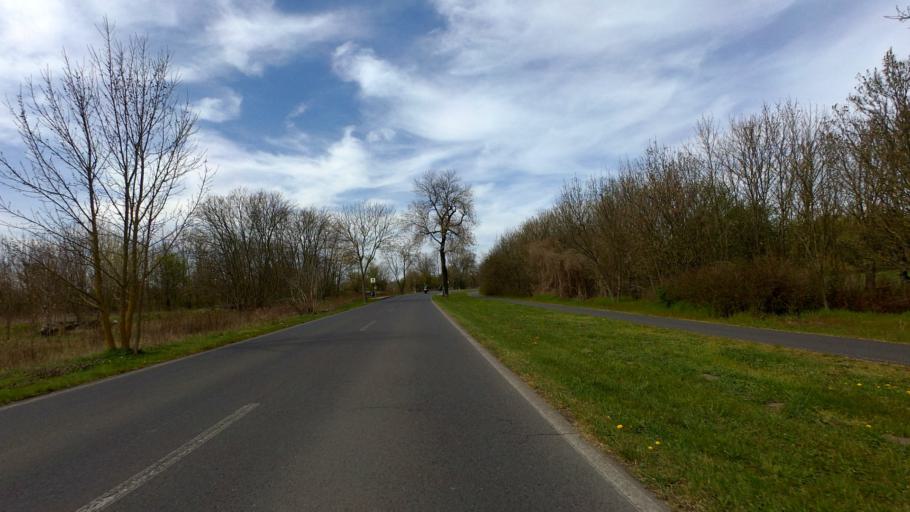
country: DE
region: Berlin
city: Gropiusstadt
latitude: 52.3753
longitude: 13.4559
